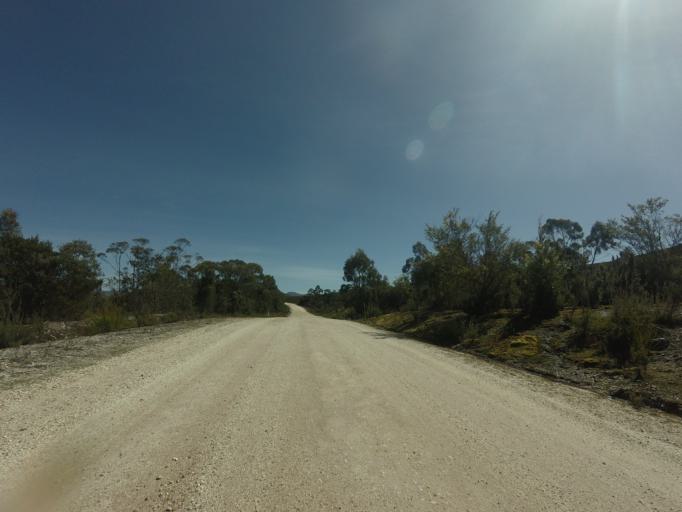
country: AU
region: Tasmania
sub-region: Huon Valley
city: Geeveston
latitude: -43.0337
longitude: 146.3088
